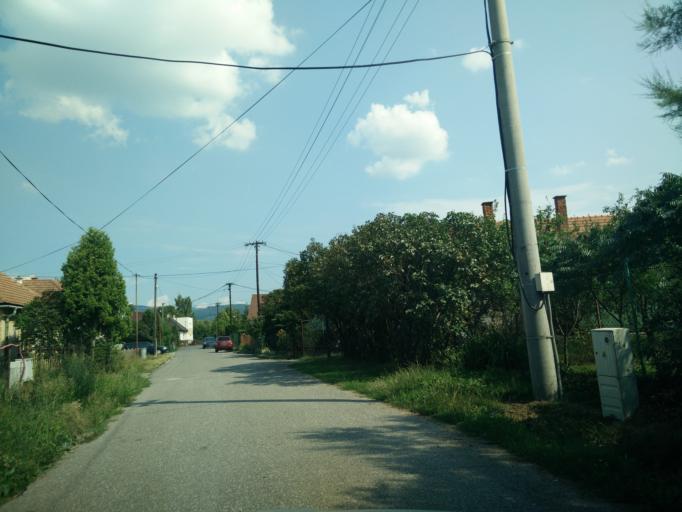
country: SK
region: Nitriansky
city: Prievidza
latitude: 48.7372
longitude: 18.5984
